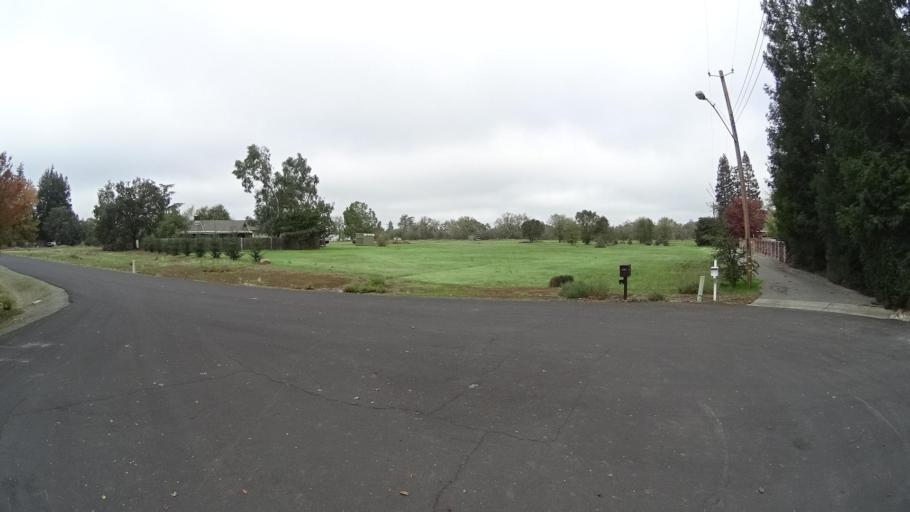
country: US
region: California
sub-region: Sacramento County
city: Wilton
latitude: 38.4305
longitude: -121.2966
